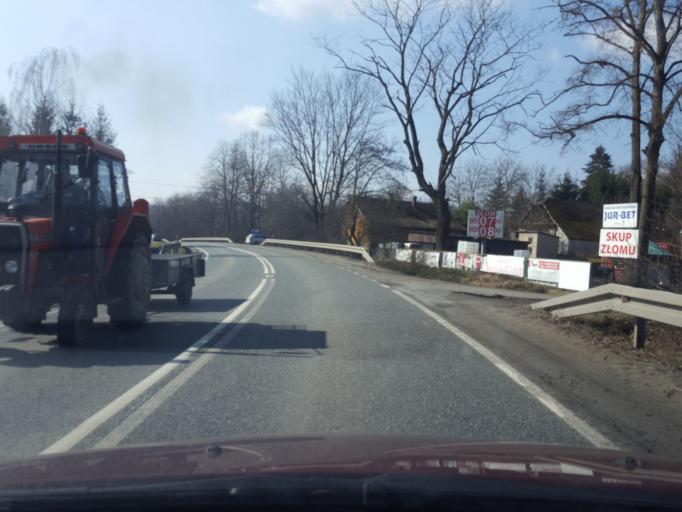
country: PL
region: Lesser Poland Voivodeship
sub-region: Powiat brzeski
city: Czchow
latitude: 49.8483
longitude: 20.6861
